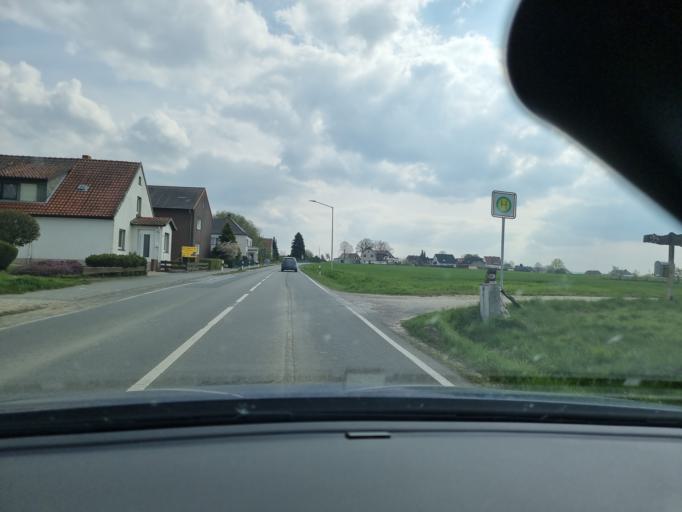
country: DE
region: North Rhine-Westphalia
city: Spenge
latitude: 52.1545
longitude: 8.4958
